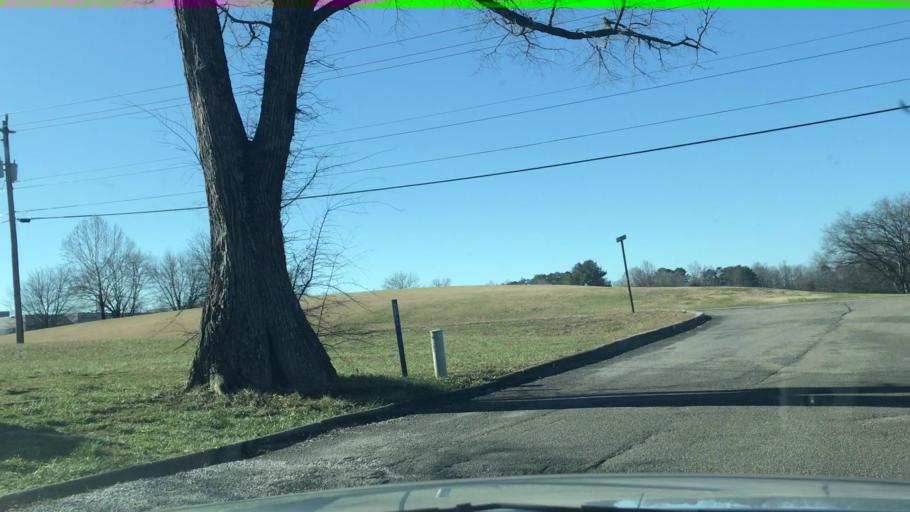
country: US
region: Tennessee
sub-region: Roane County
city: Midtown
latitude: 35.8834
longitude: -84.6170
